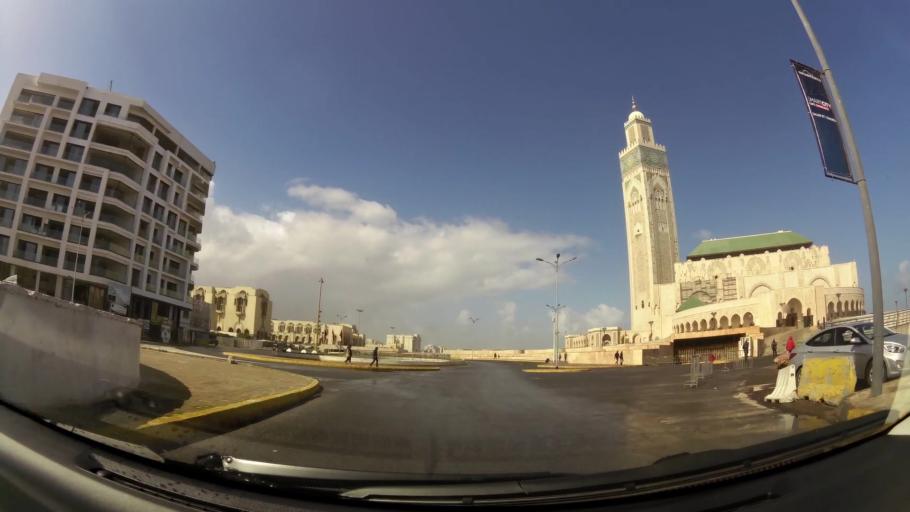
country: MA
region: Grand Casablanca
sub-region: Casablanca
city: Casablanca
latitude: 33.6082
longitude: -7.6295
